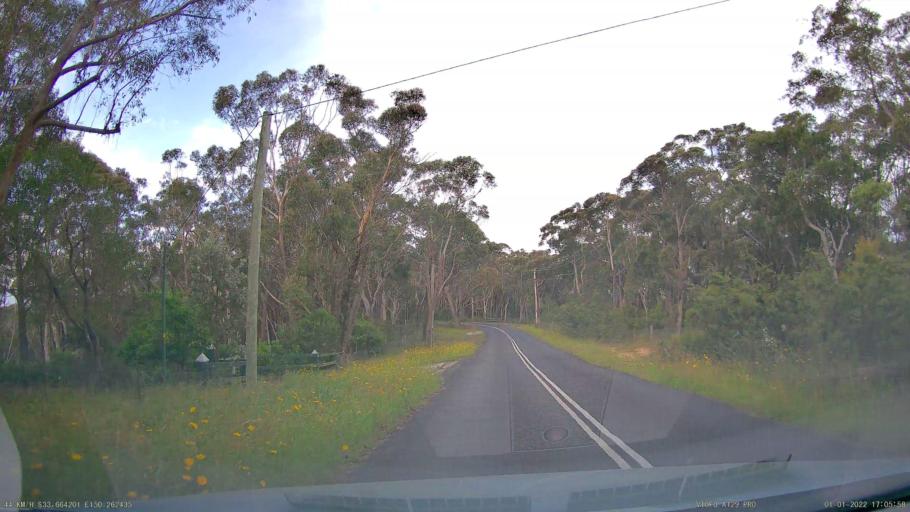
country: AU
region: New South Wales
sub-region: Blue Mountains Municipality
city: Blackheath
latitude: -33.6641
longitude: 150.2625
